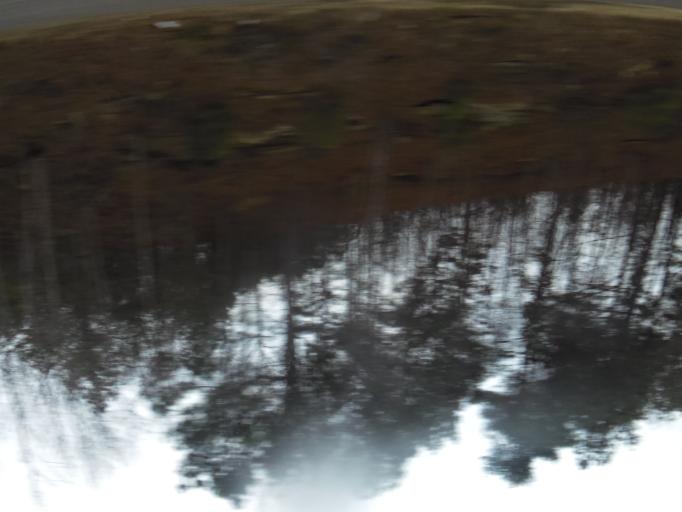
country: US
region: Alabama
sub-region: Blount County
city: Smoke Rise
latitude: 33.8525
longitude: -86.8290
